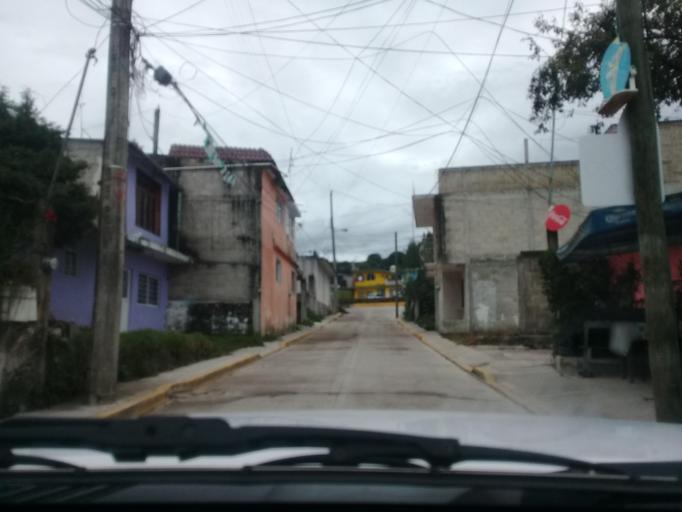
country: MX
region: Veracruz
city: Rafael Lucio
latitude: 19.5963
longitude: -96.9884
